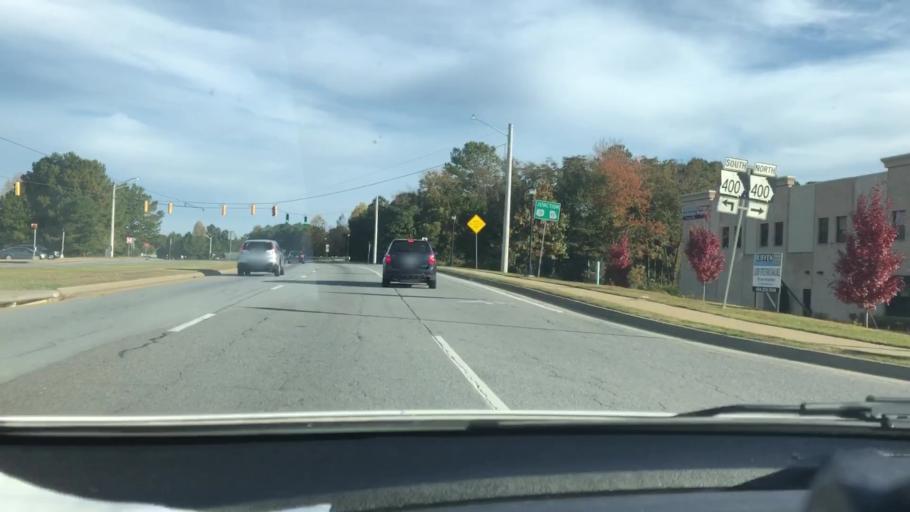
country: US
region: Georgia
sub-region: Forsyth County
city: Cumming
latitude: 34.1557
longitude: -84.1734
